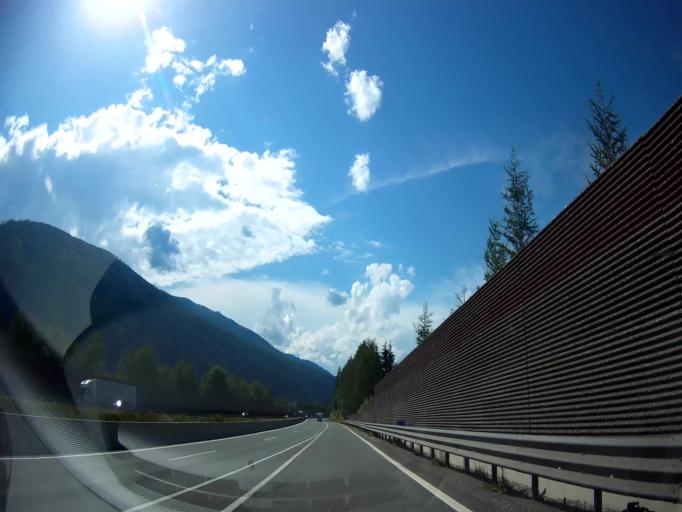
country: AT
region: Salzburg
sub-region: Politischer Bezirk Tamsweg
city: Sankt Michael im Lungau
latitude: 47.0979
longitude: 13.6068
